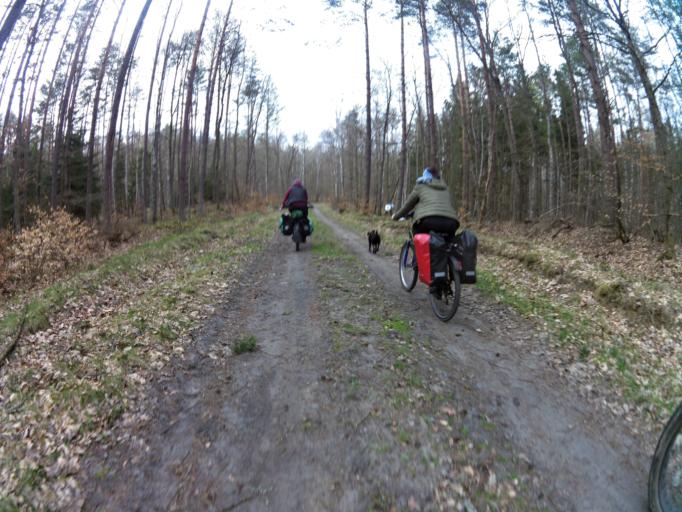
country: PL
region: West Pomeranian Voivodeship
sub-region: Powiat szczecinecki
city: Bialy Bor
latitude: 53.8956
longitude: 16.7173
